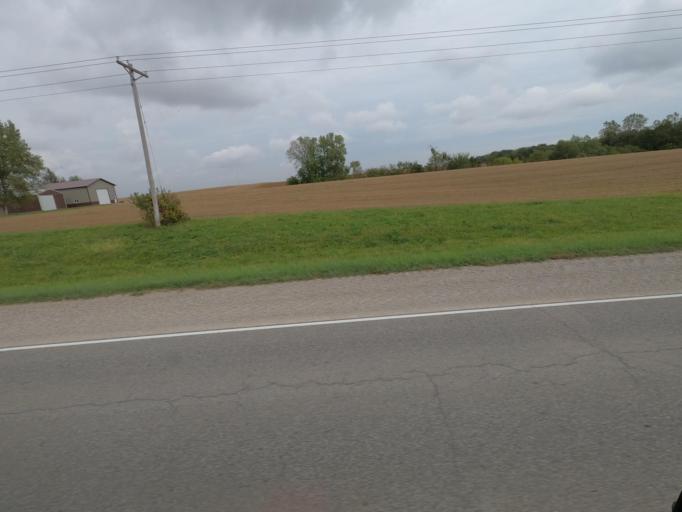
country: US
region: Iowa
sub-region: Wapello County
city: Ottumwa
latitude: 40.9435
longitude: -92.2270
